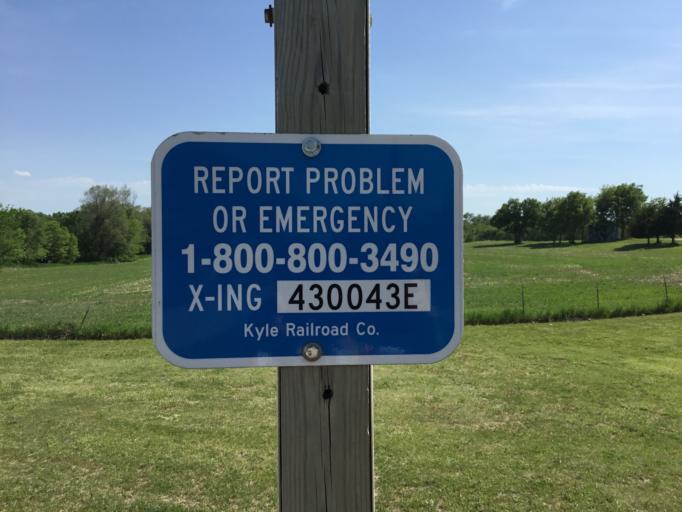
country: US
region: Kansas
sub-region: Mitchell County
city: Beloit
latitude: 39.4592
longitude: -98.1233
